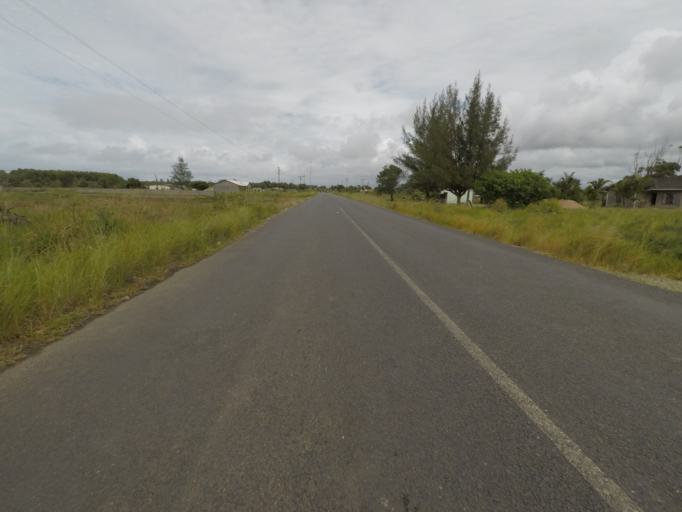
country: ZA
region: KwaZulu-Natal
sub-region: uThungulu District Municipality
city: eSikhawini
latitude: -28.9102
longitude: 31.8692
